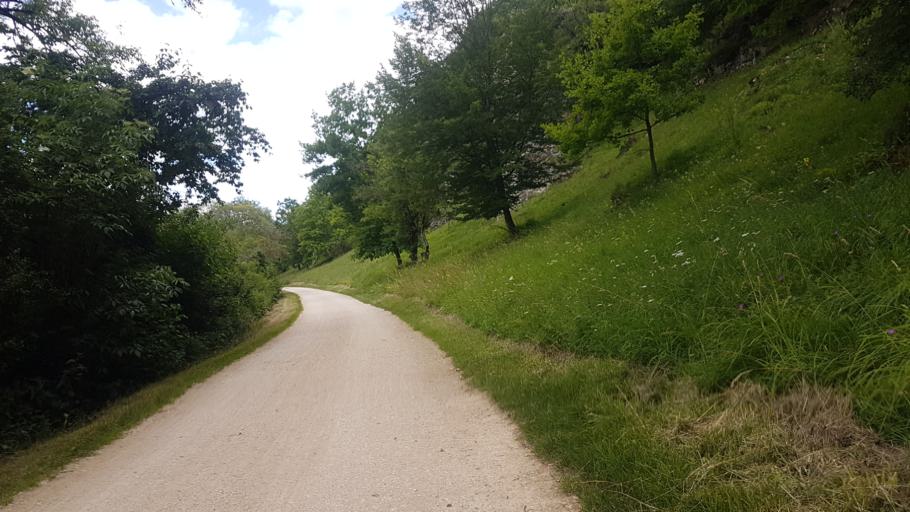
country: DE
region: Bavaria
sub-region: Regierungsbezirk Mittelfranken
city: Solnhofen
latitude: 48.8720
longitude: 11.0351
